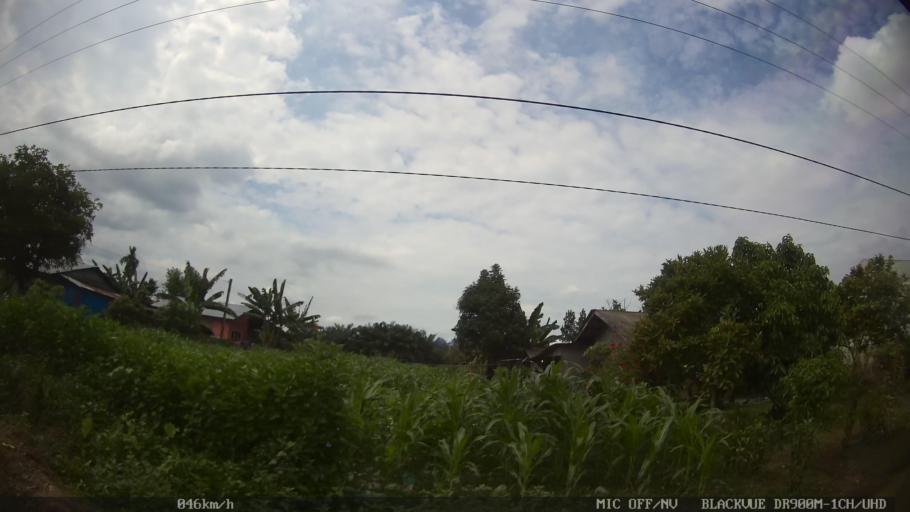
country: ID
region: North Sumatra
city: Sunggal
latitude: 3.6360
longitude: 98.5989
